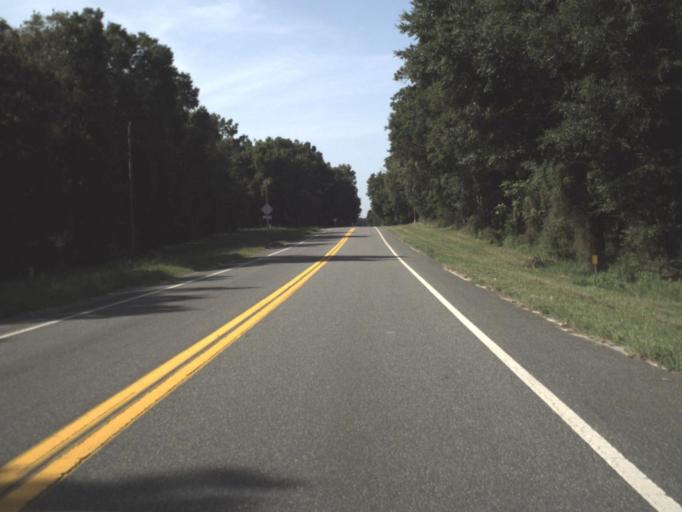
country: US
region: Florida
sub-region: Alachua County
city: High Springs
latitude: 29.9863
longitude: -82.7100
